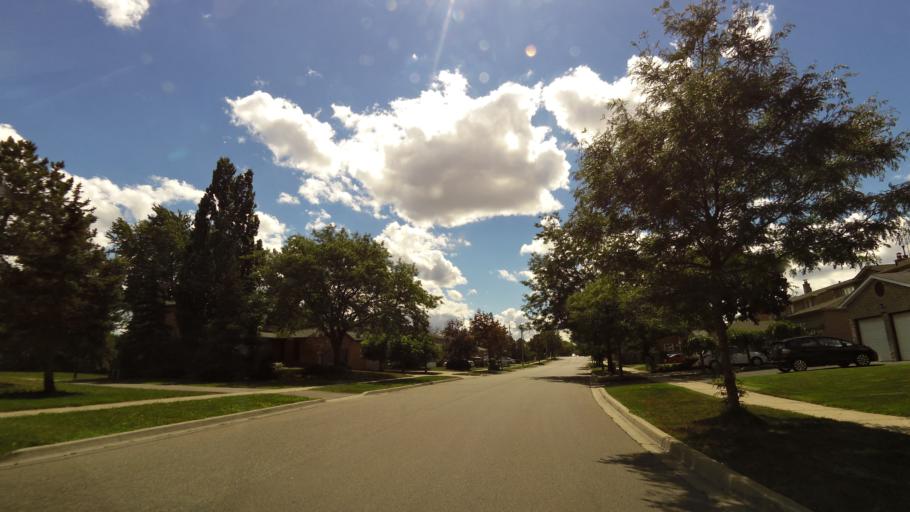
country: CA
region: Ontario
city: Mississauga
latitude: 43.6208
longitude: -79.6180
